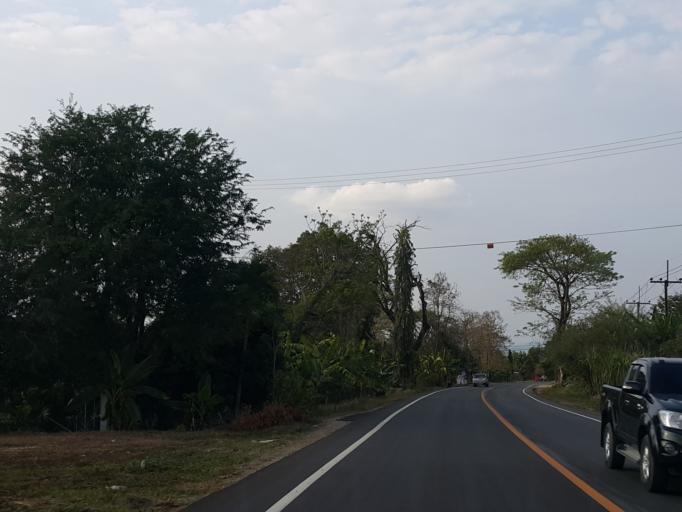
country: TH
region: Lampang
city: Lampang
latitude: 18.4883
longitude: 99.4723
